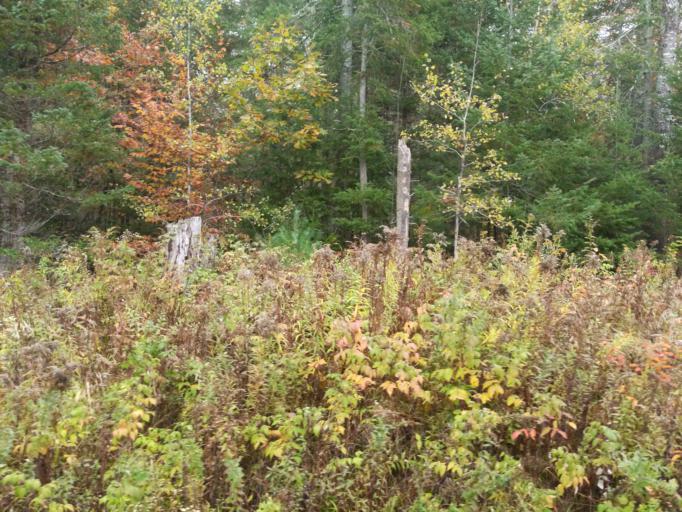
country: US
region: Maine
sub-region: Lincoln County
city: Whitefield
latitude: 44.0920
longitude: -69.6251
